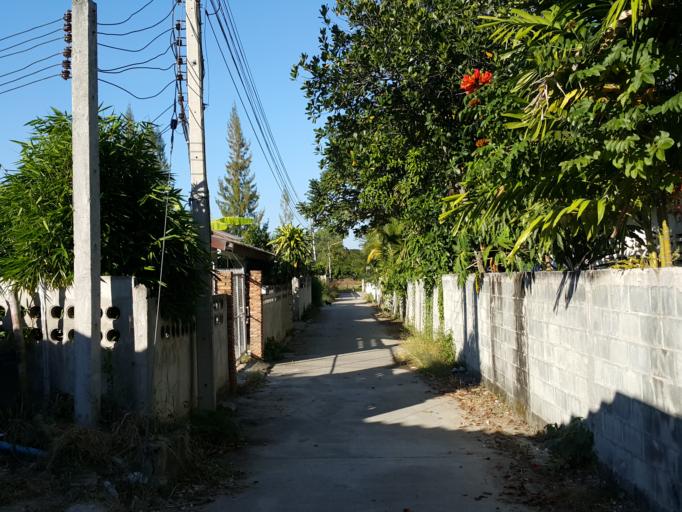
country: TH
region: Chiang Mai
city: San Kamphaeng
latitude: 18.7761
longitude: 99.0880
